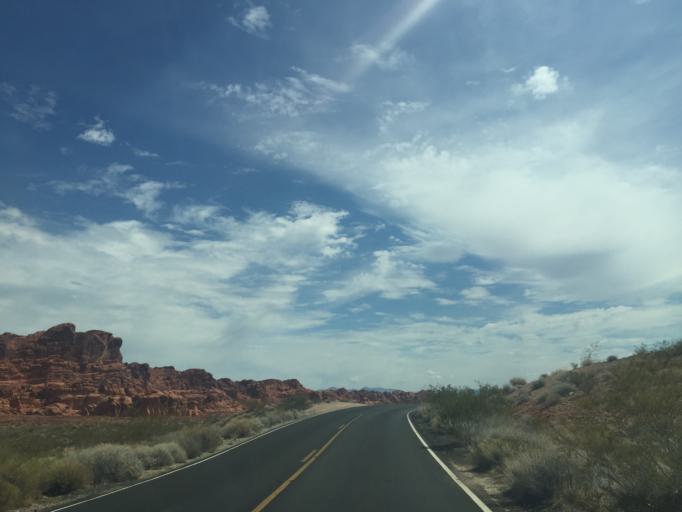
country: US
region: Nevada
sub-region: Clark County
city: Moapa Valley
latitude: 36.4252
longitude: -114.5295
